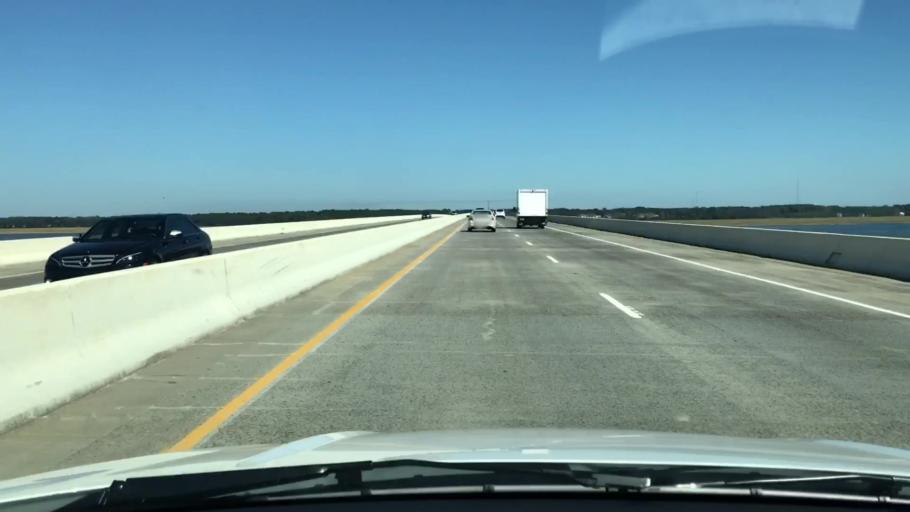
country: US
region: South Carolina
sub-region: Beaufort County
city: Shell Point
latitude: 32.3837
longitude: -80.7843
